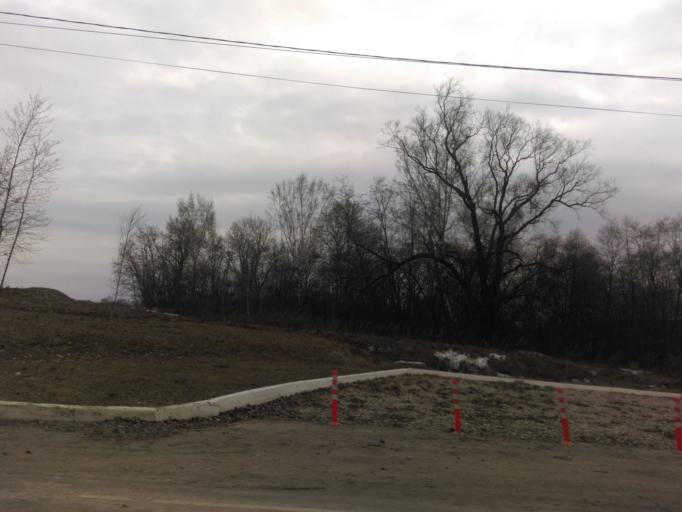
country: RU
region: Moskovskaya
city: Gorki Vtoryye
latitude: 55.7154
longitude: 37.1070
